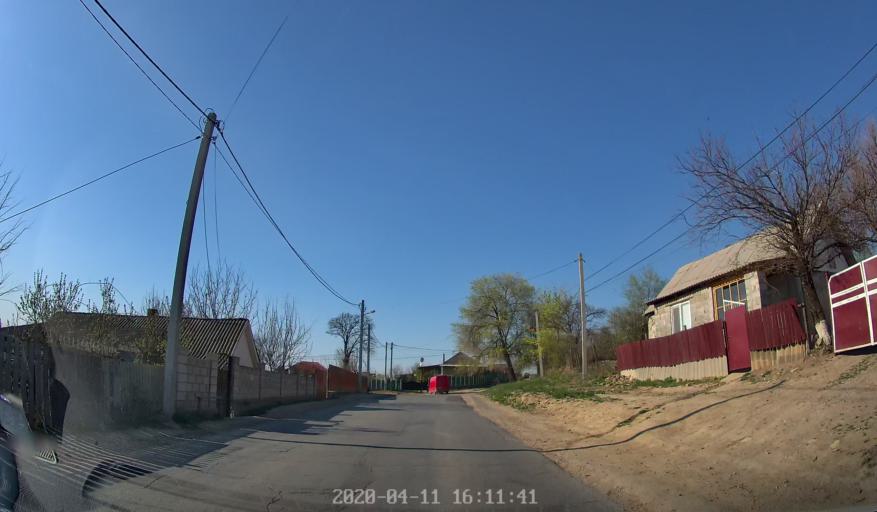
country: MD
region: Chisinau
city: Vadul lui Voda
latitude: 47.0691
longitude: 29.1282
